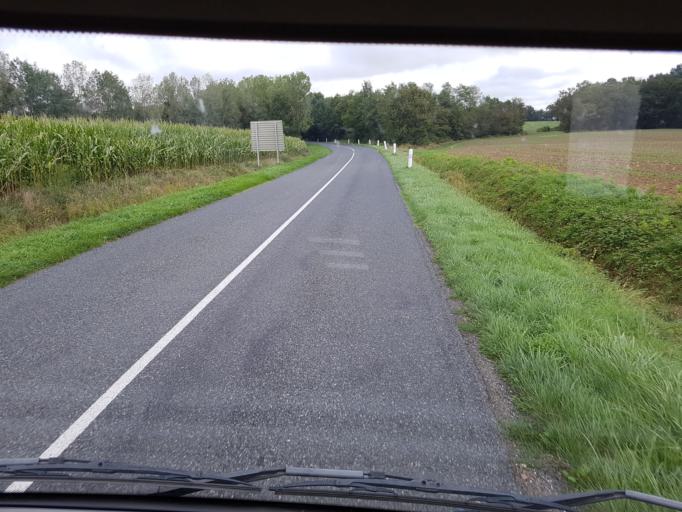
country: FR
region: Rhone-Alpes
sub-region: Departement de l'Ain
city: Perouges
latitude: 45.9237
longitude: 5.1306
